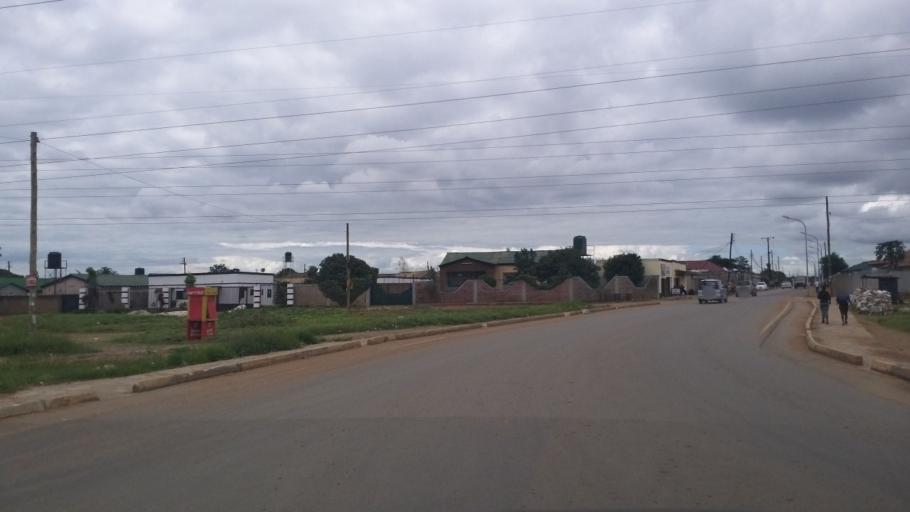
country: ZM
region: Lusaka
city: Lusaka
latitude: -15.4456
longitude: 28.3053
